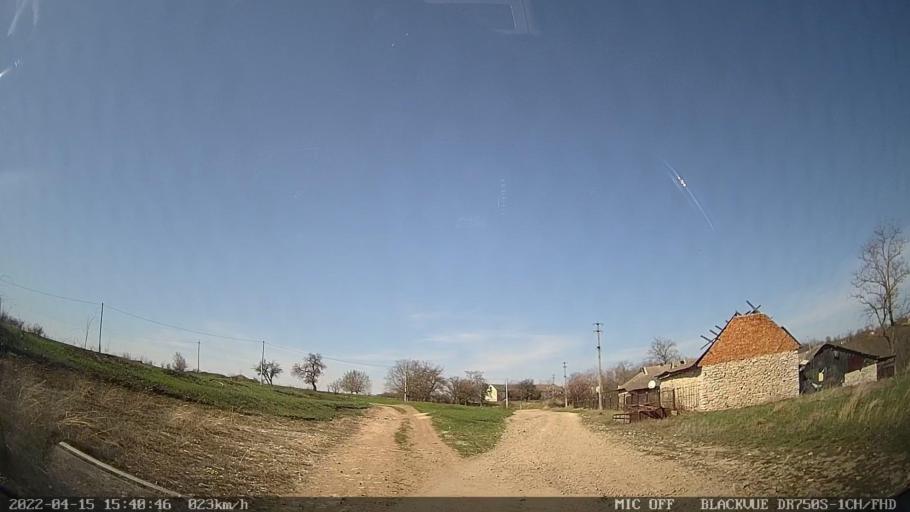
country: MD
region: Raionul Ocnita
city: Otaci
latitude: 48.3570
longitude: 27.9248
